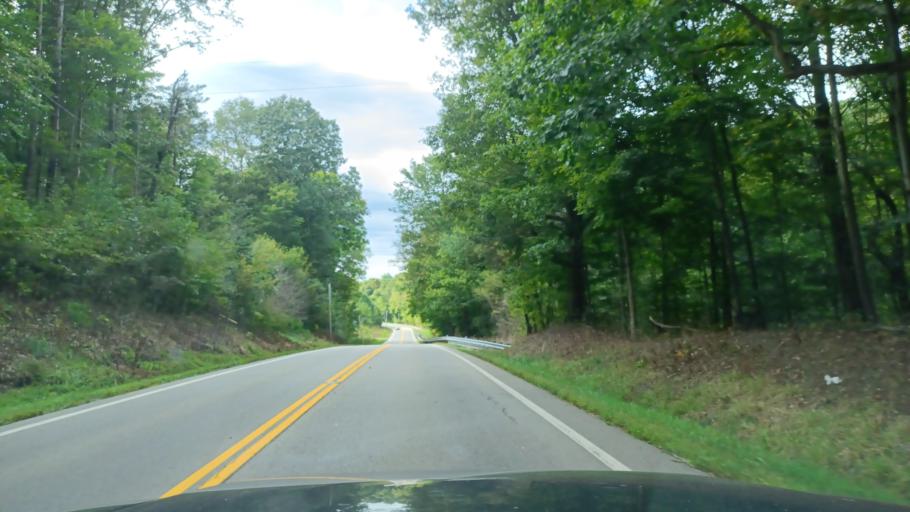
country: US
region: Ohio
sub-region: Vinton County
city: McArthur
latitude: 39.2394
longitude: -82.3491
